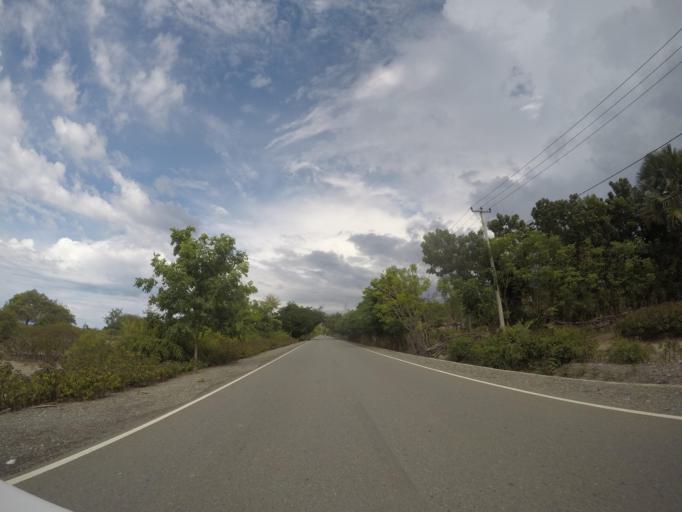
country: TL
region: Liquica
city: Maubara
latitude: -8.6063
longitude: 125.2270
